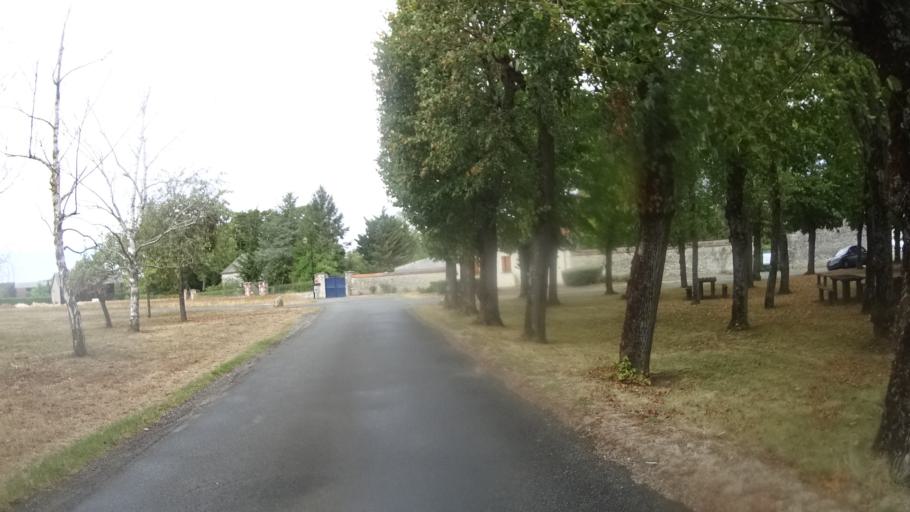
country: FR
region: Centre
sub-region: Departement du Loiret
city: Boynes
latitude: 48.1998
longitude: 2.4058
